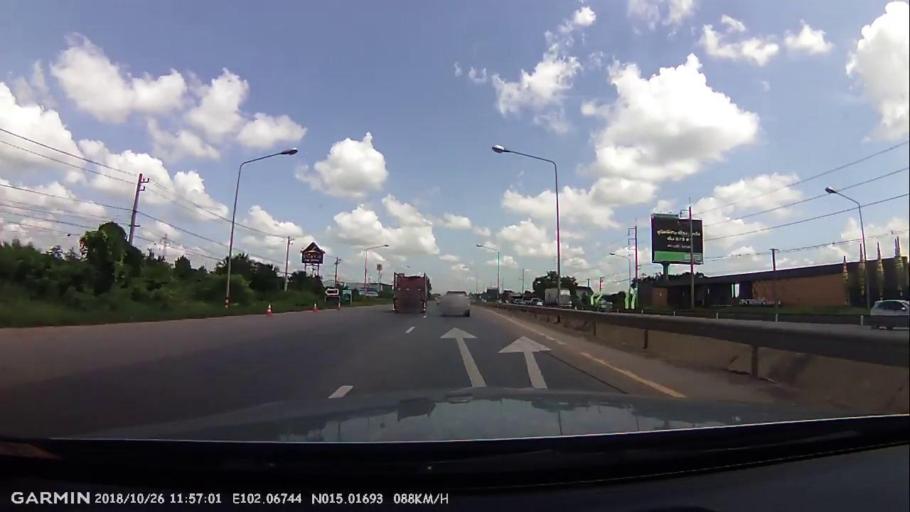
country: TH
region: Nakhon Ratchasima
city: Nakhon Ratchasima
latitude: 15.0170
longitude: 102.0676
